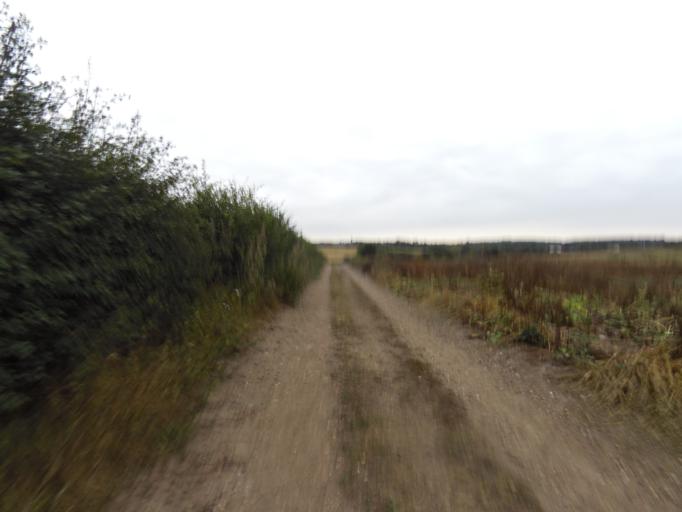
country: GB
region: England
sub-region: Hertfordshire
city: Radlett
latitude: 51.7160
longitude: -0.3139
